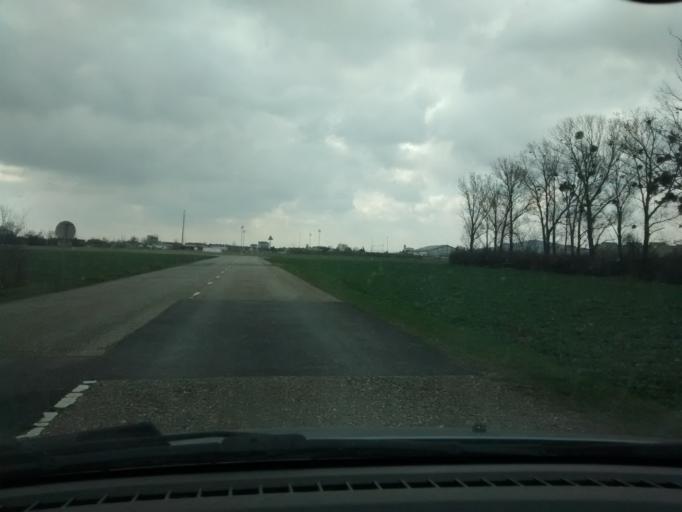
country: AT
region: Lower Austria
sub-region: Politischer Bezirk Modling
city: Wiener Neudorf
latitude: 48.0958
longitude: 16.3178
